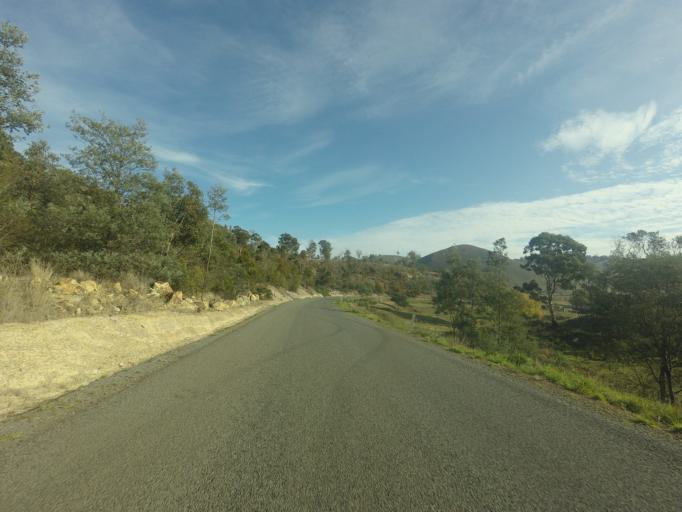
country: AU
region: Tasmania
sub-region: Brighton
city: Bridgewater
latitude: -42.5156
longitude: 147.4163
